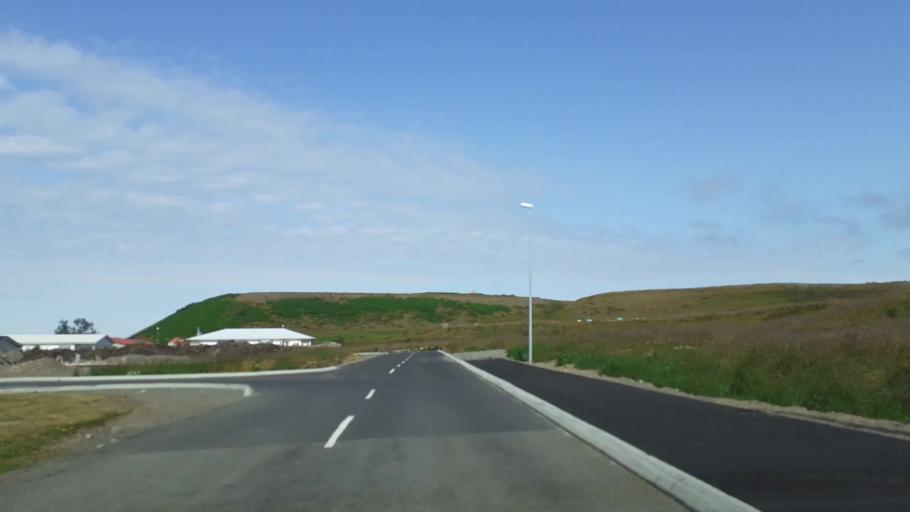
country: IS
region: Northwest
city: Saudarkrokur
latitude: 65.6637
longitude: -20.2838
